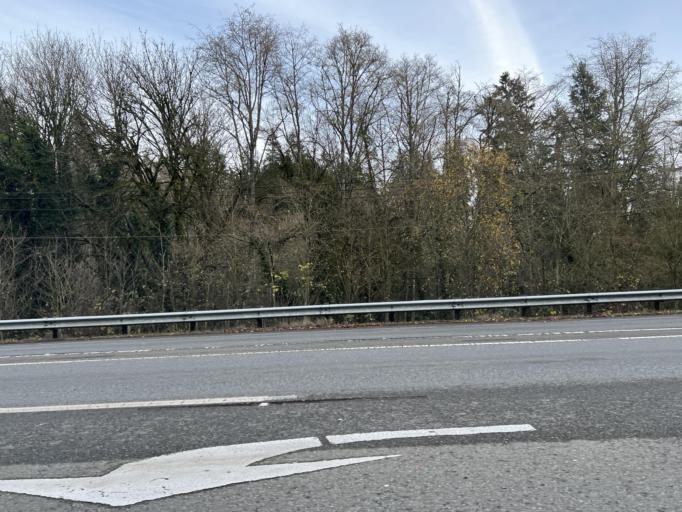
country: US
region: Washington
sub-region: Kitsap County
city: Bainbridge Island
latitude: 47.6532
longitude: -122.5211
